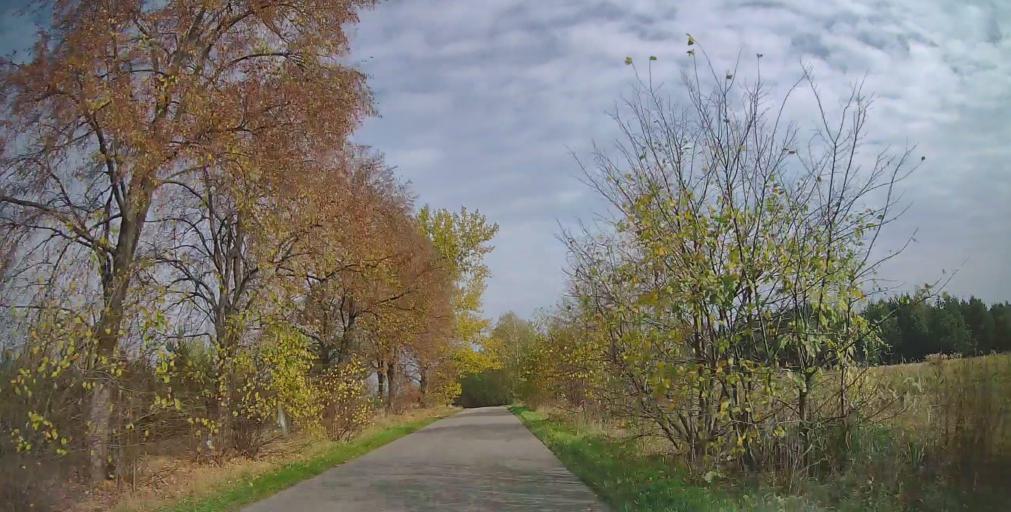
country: PL
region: Masovian Voivodeship
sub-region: Powiat bialobrzeski
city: Wysmierzyce
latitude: 51.6500
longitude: 20.7656
